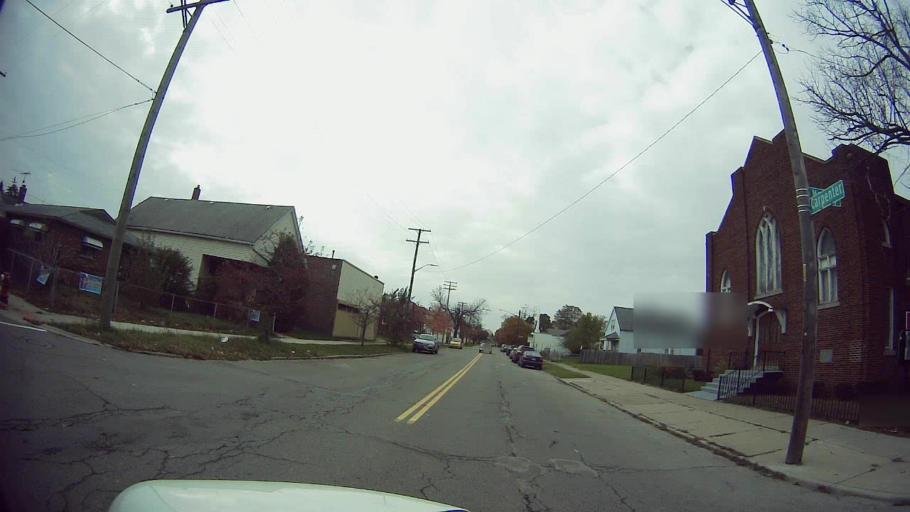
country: US
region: Michigan
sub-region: Wayne County
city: Hamtramck
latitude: 42.4054
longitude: -83.0668
